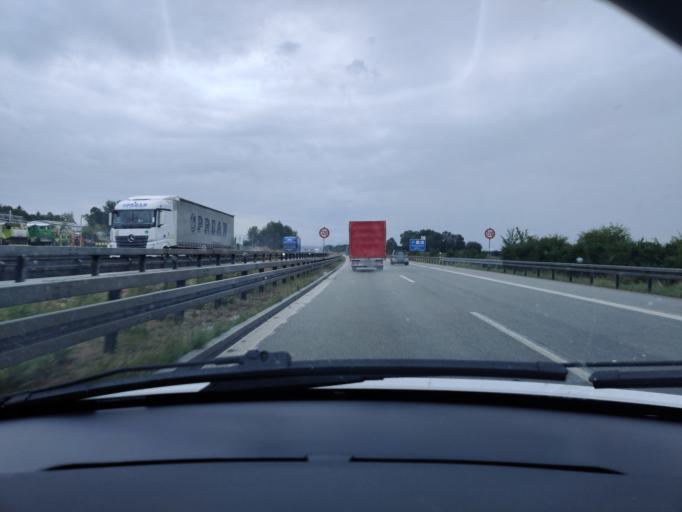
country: DE
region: Bavaria
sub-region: Upper Palatinate
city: Pfreimd
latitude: 49.4837
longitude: 12.1887
